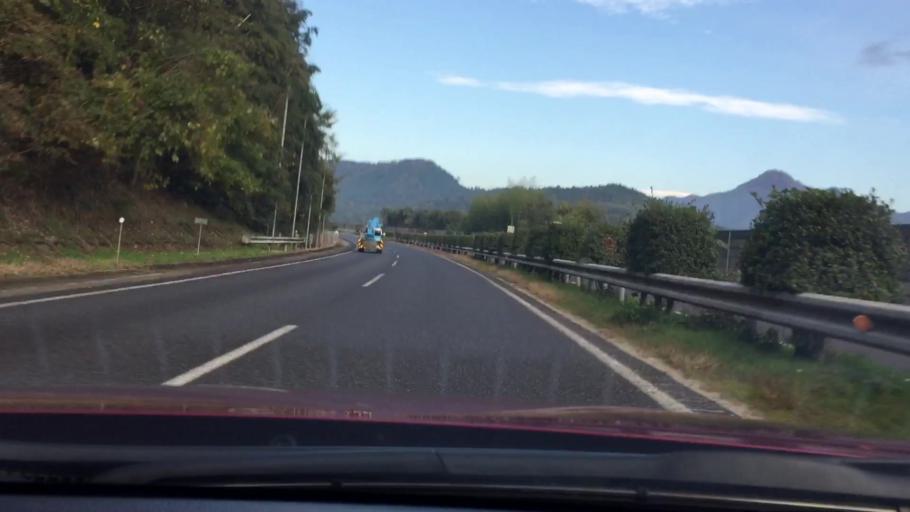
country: JP
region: Hyogo
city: Yamazakicho-nakabirose
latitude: 34.9668
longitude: 134.6763
